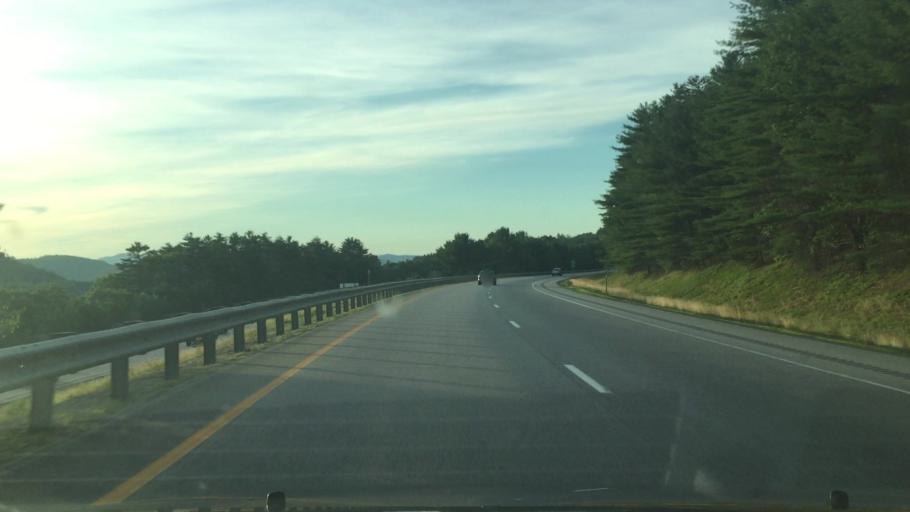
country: US
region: New Hampshire
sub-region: Grafton County
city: Ashland
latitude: 43.7032
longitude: -71.6495
